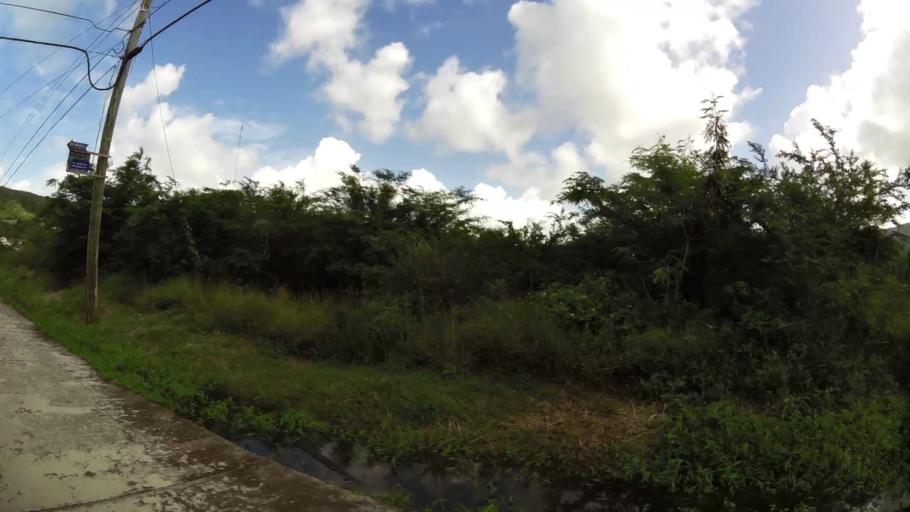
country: AG
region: Saint Mary
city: Bolands
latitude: 17.0750
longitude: -61.8745
